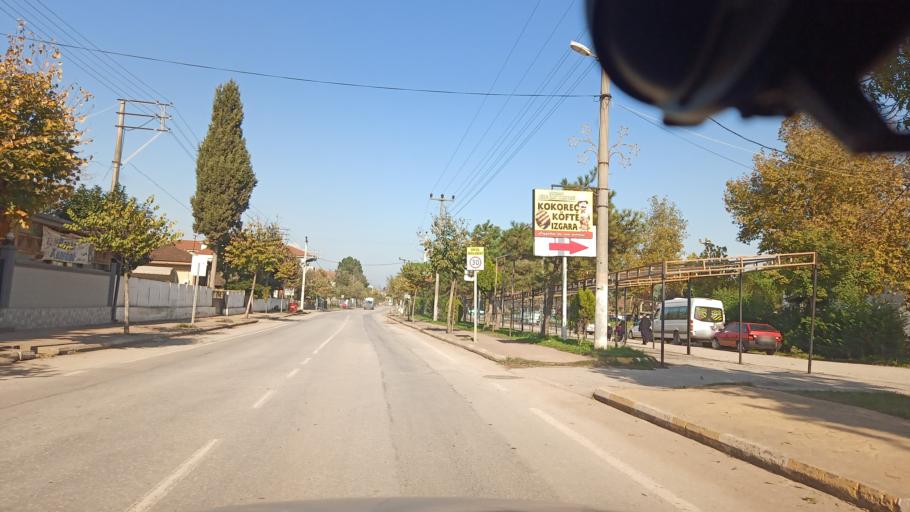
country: TR
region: Sakarya
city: Sogutlu
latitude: 40.8956
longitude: 30.4693
